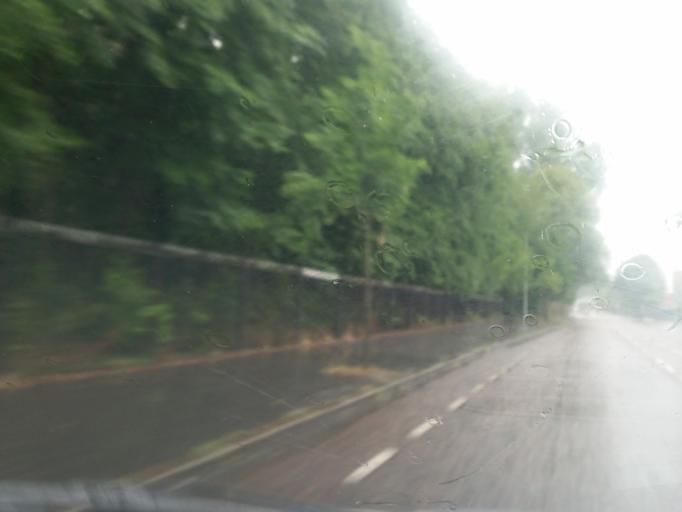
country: GB
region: Northern Ireland
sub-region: Castlereagh District
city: Castlereagh
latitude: 54.6111
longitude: -5.8653
